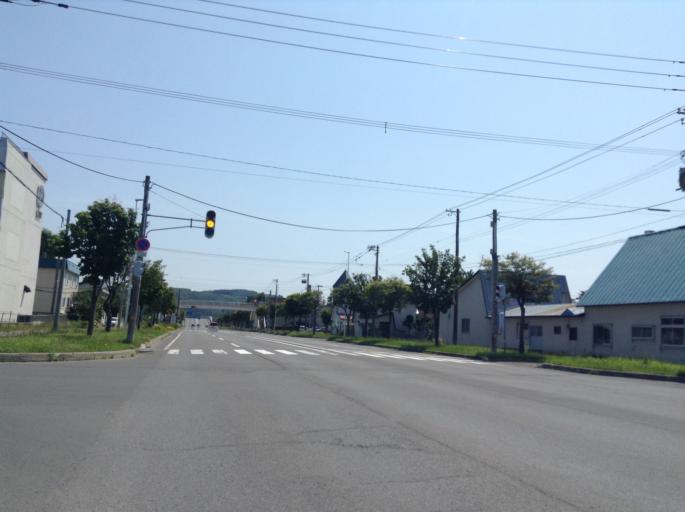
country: JP
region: Hokkaido
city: Nayoro
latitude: 44.3564
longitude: 142.4586
